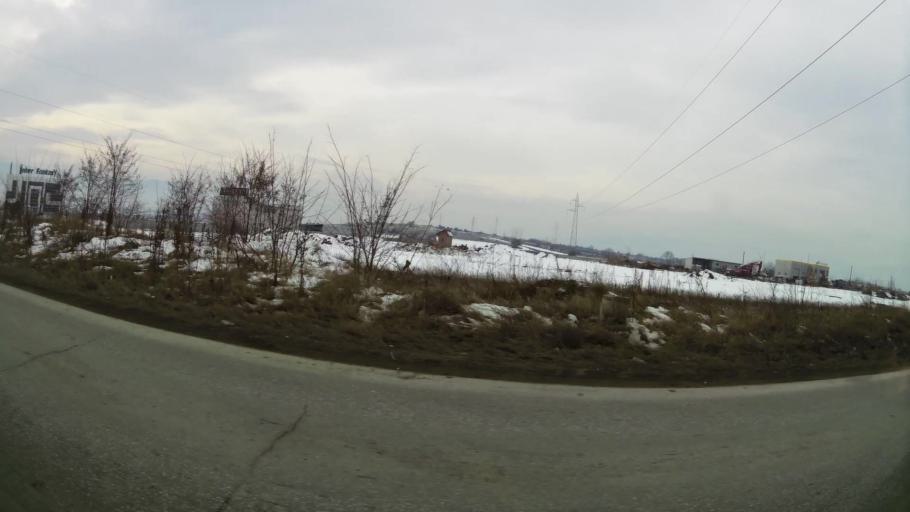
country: MK
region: Suto Orizari
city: Suto Orizare
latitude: 42.0478
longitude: 21.3860
